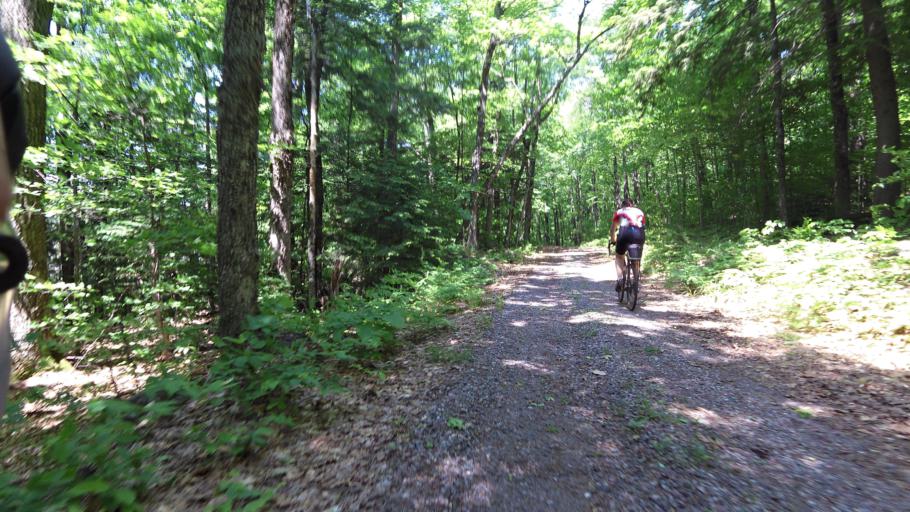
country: CA
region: Quebec
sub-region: Outaouais
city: Wakefield
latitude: 45.5776
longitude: -75.9470
